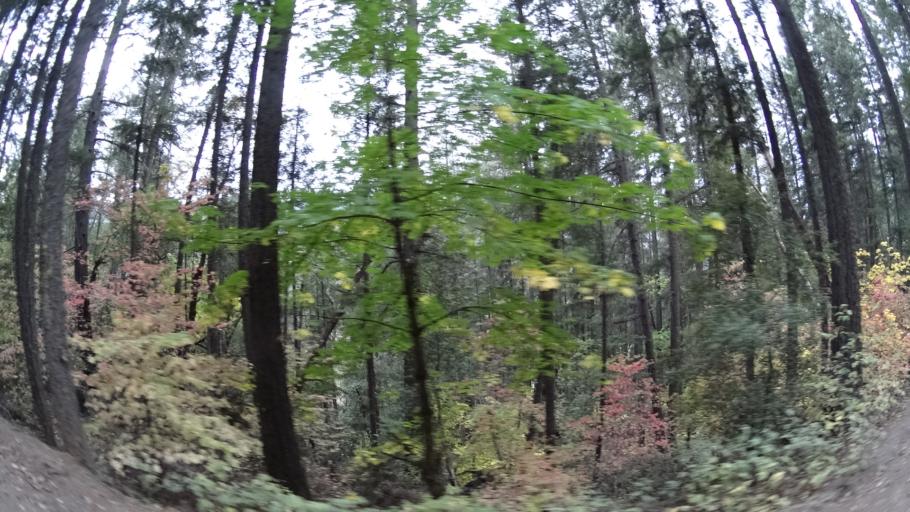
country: US
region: California
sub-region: Siskiyou County
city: Happy Camp
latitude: 41.7870
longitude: -123.3354
